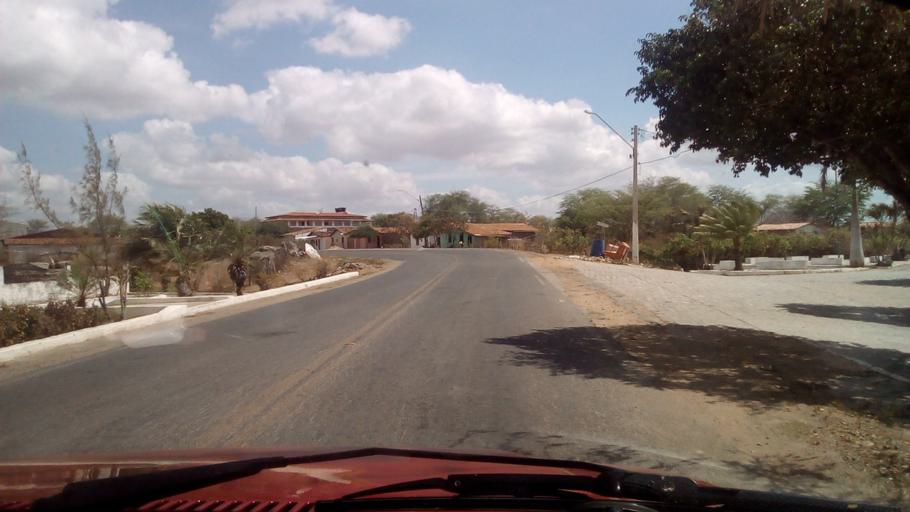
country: BR
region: Paraiba
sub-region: Dona Ines
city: Dona Ines
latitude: -6.5366
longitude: -35.6535
